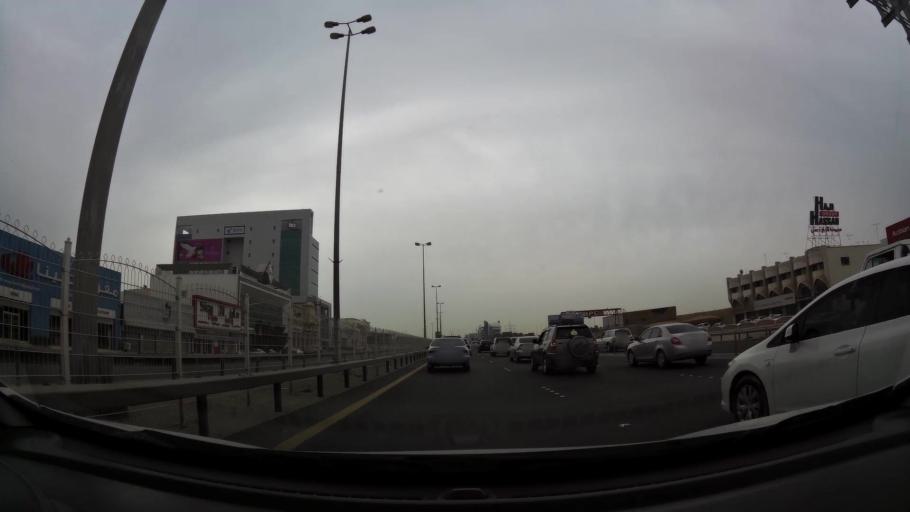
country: BH
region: Northern
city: Madinat `Isa
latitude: 26.1912
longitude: 50.5355
